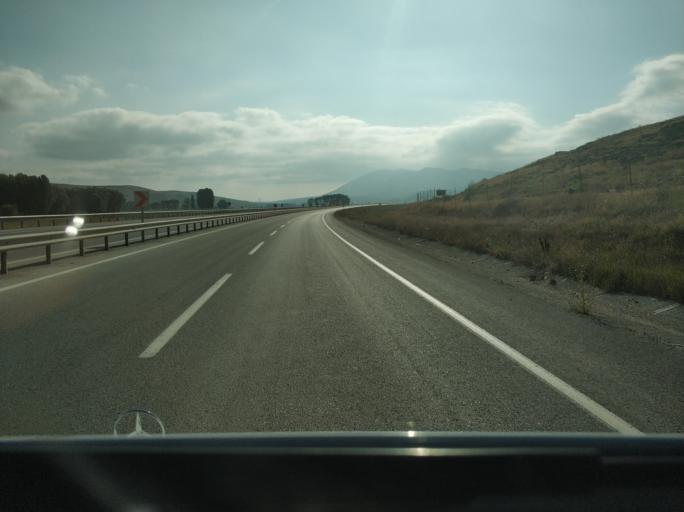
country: TR
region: Sivas
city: Yildizeli
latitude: 39.8510
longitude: 36.5015
